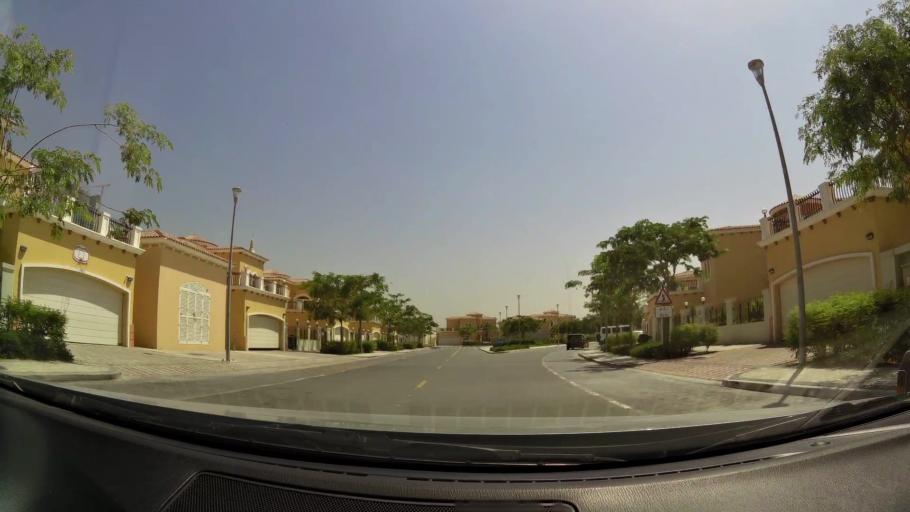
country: AE
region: Dubai
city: Dubai
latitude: 25.0587
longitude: 55.1439
